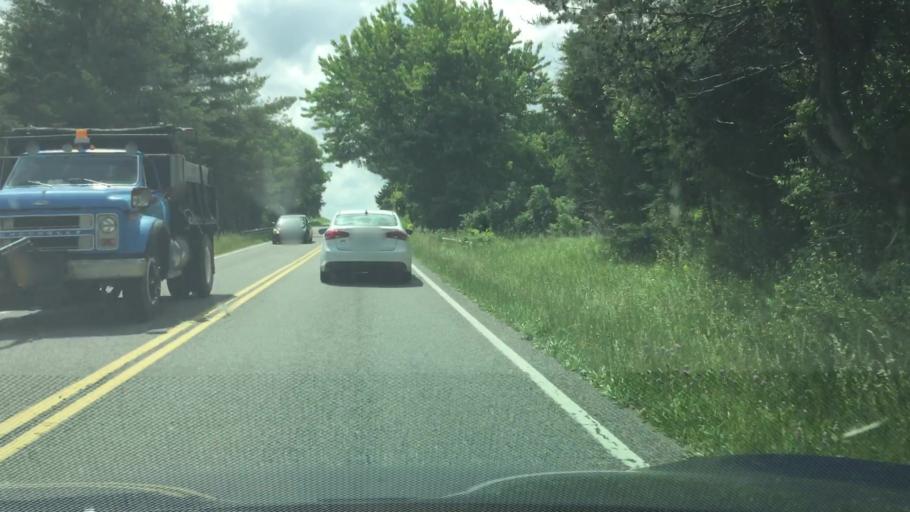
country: US
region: Virginia
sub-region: Pulaski County
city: Dublin
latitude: 37.0800
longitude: -80.6730
